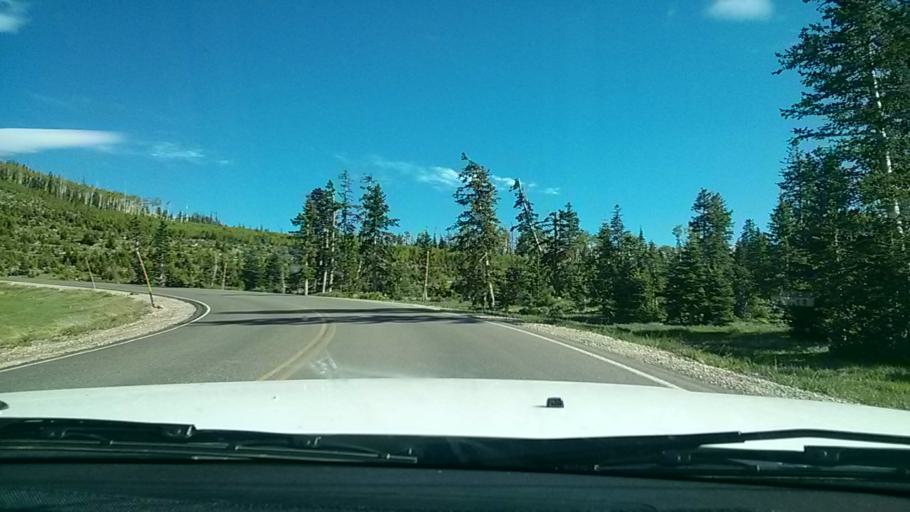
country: US
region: Utah
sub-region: Iron County
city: Parowan
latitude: 37.6827
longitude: -112.8553
